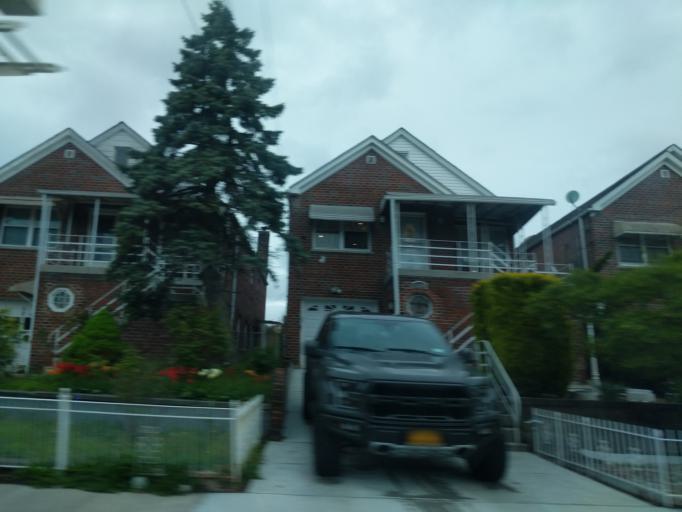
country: US
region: New York
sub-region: Bronx
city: The Bronx
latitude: 40.8599
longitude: -73.8477
